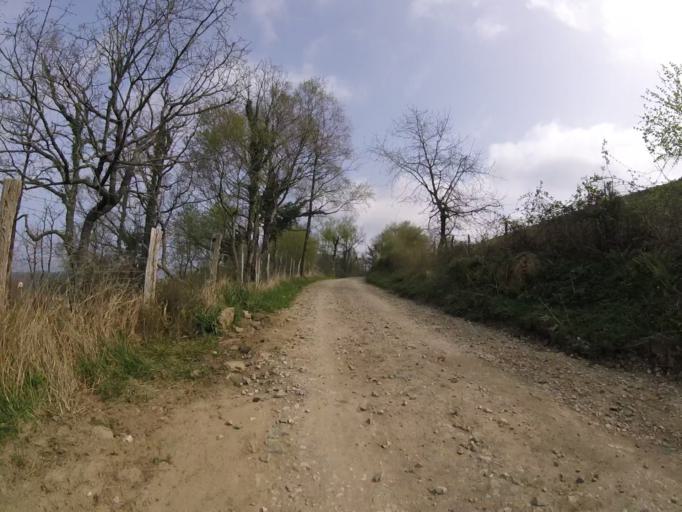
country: ES
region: Basque Country
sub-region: Provincia de Guipuzcoa
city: Zizurkil
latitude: 43.2352
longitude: -2.0856
